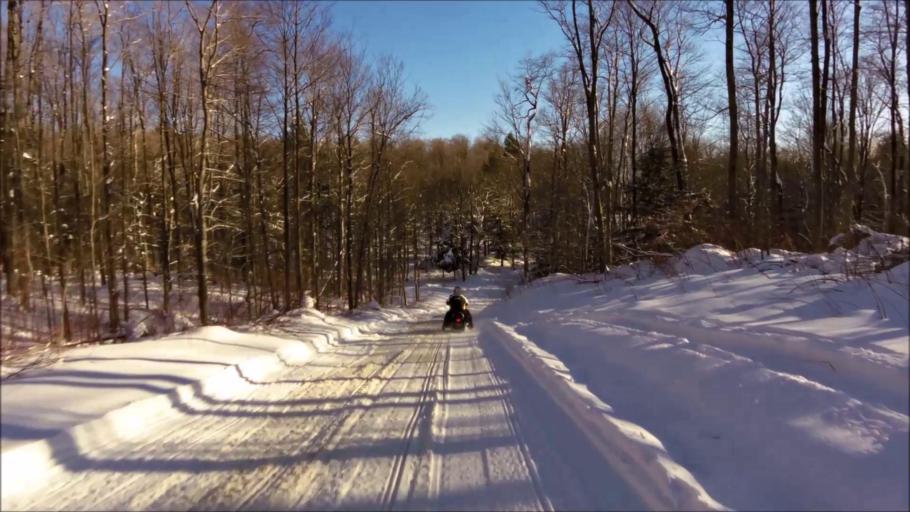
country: US
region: New York
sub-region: Chautauqua County
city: Mayville
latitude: 42.2803
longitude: -79.4141
